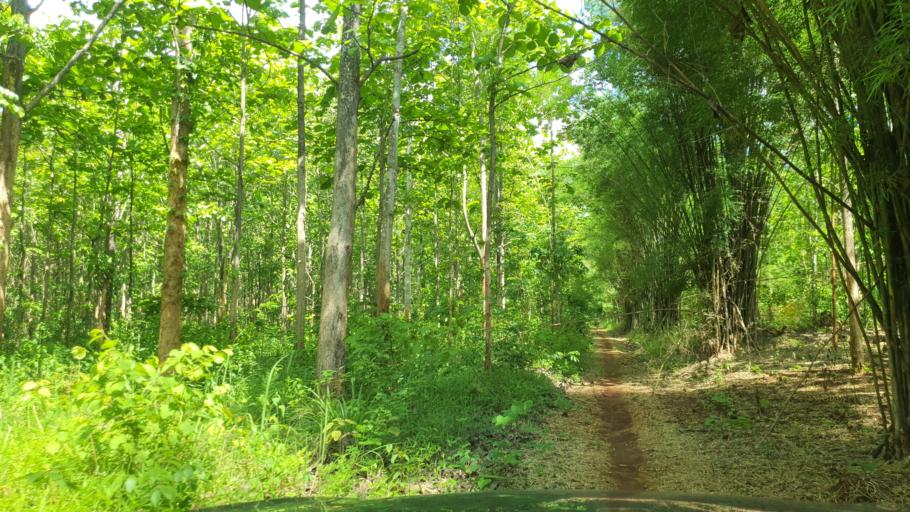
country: TH
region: Chiang Mai
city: Mae Taeng
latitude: 19.0770
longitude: 99.0971
